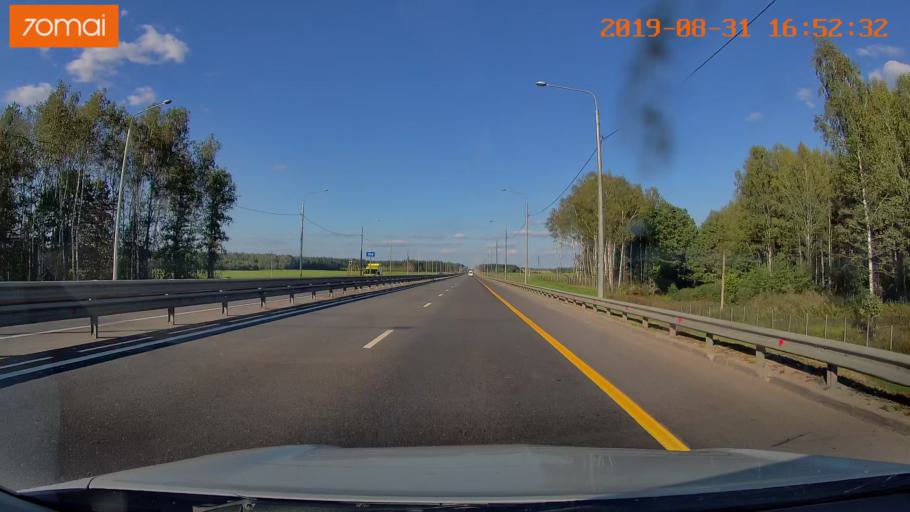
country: RU
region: Kaluga
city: Detchino
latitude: 54.7425
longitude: 36.1932
